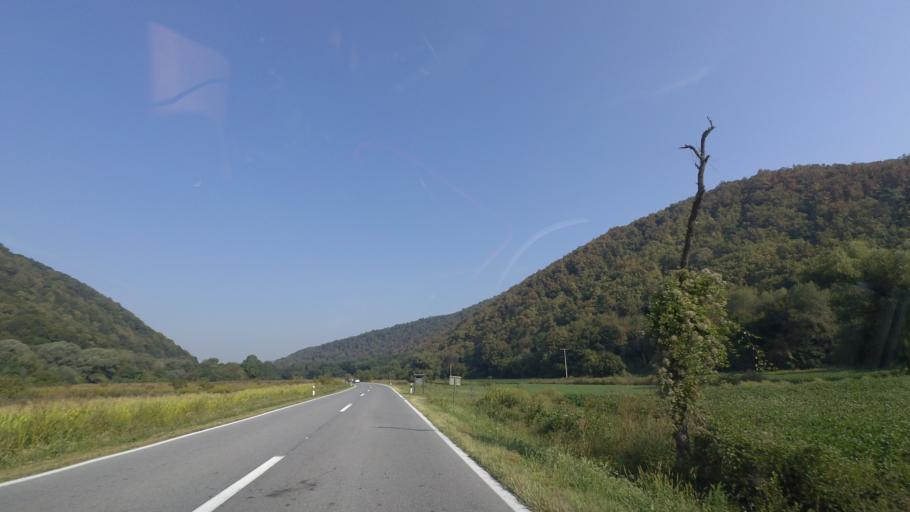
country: HR
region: Pozesko-Slavonska
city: Velika
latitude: 45.4323
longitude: 17.5005
